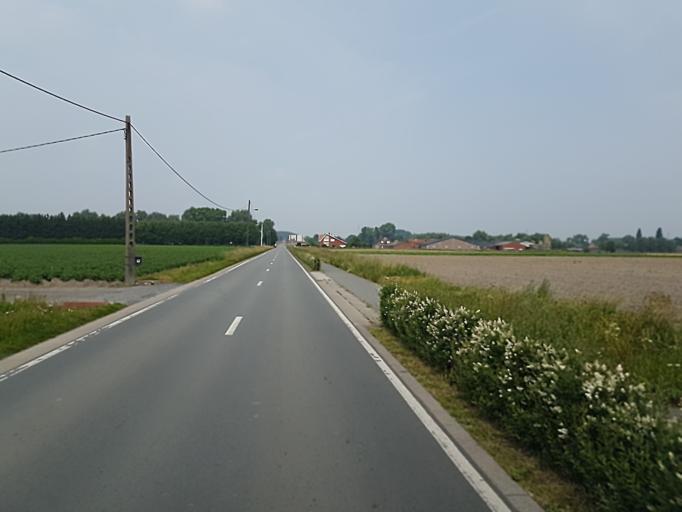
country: BE
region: Flanders
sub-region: Provincie West-Vlaanderen
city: Ardooie
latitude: 50.9504
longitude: 3.2008
